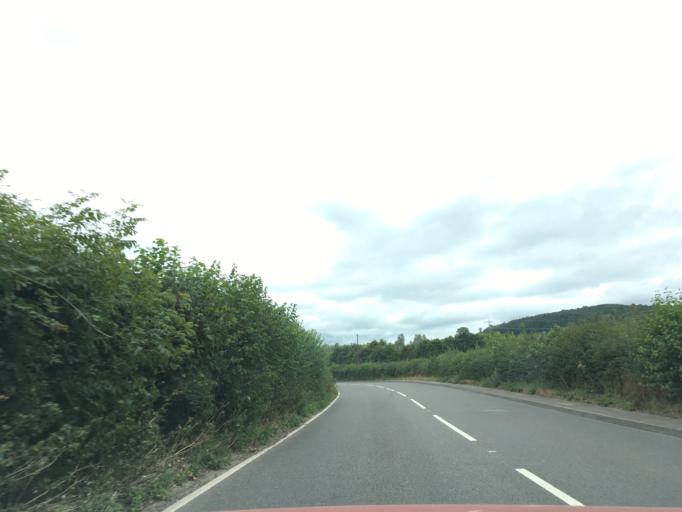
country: GB
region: Wales
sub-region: Monmouthshire
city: Abergavenny
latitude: 51.8038
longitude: -3.0079
